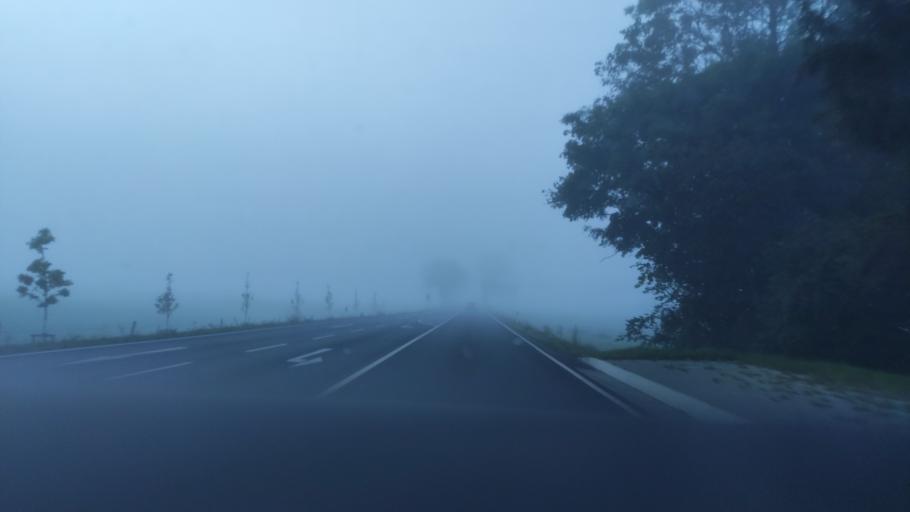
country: DE
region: Mecklenburg-Vorpommern
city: Grabowhofe
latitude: 53.5870
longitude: 12.6249
